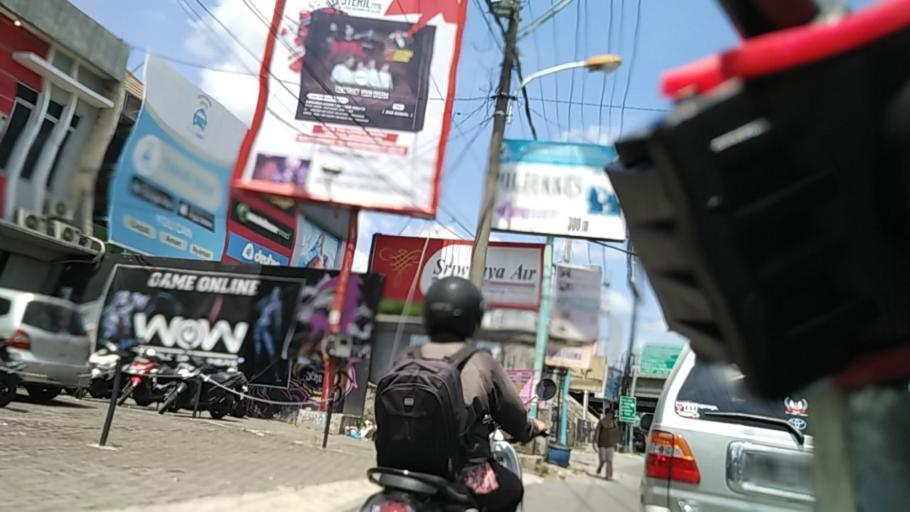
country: ID
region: Central Java
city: Semarang
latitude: -7.0539
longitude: 110.4306
